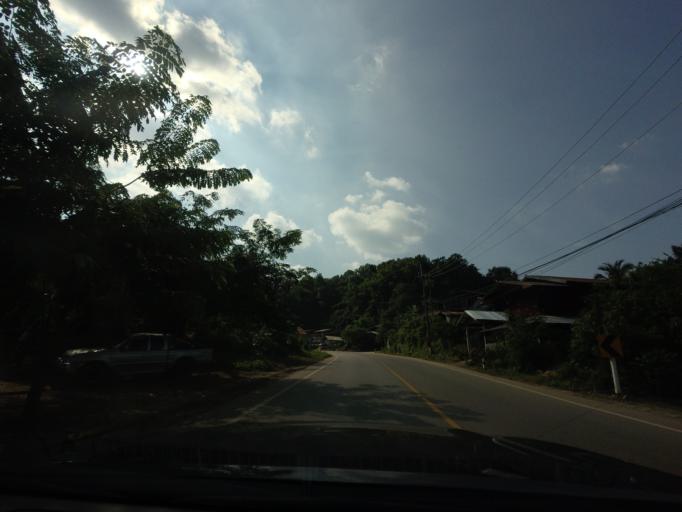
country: TH
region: Nan
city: Santi Suk
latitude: 18.9177
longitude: 100.8762
